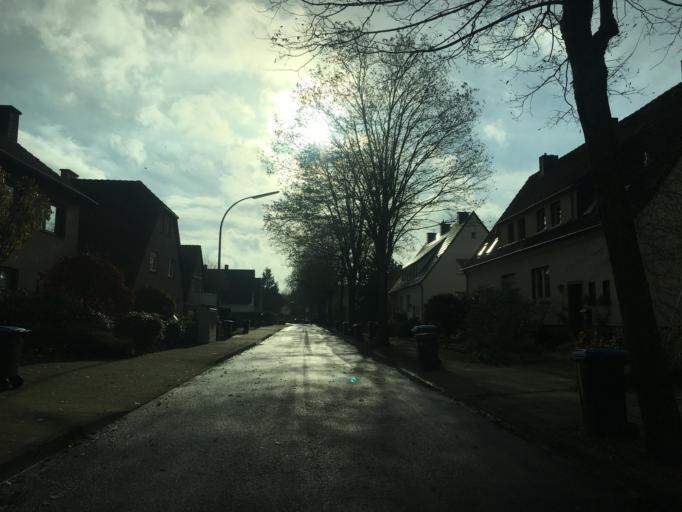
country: DE
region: North Rhine-Westphalia
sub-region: Regierungsbezirk Munster
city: Steinfurt
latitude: 52.1459
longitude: 7.3265
